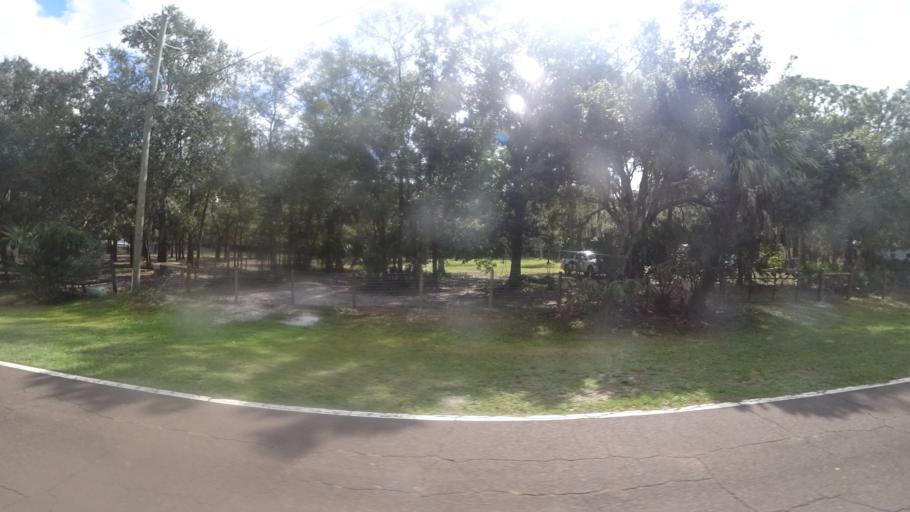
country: US
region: Florida
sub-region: Hillsborough County
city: Ruskin
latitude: 27.6495
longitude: -82.3966
